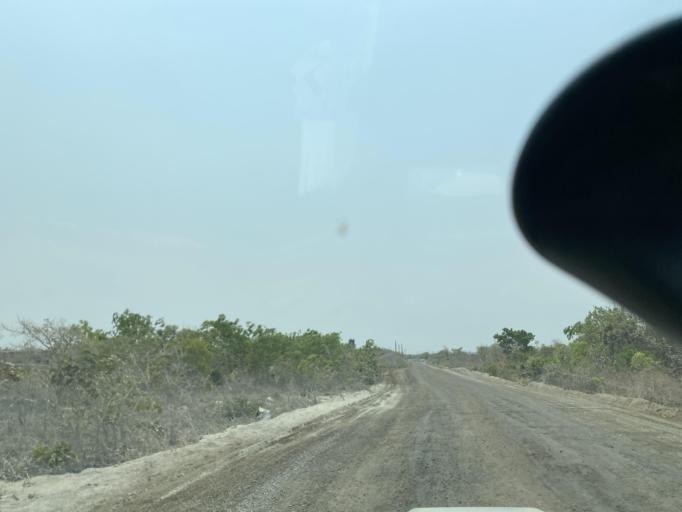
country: ZM
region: Lusaka
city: Lusaka
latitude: -15.5366
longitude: 28.4476
